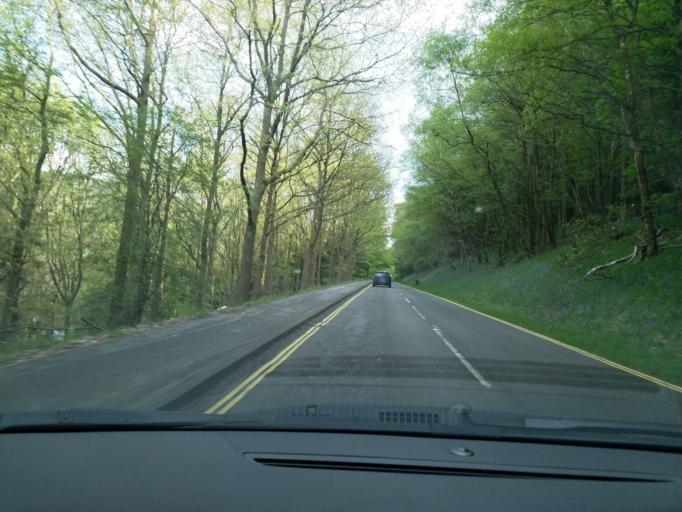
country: GB
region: England
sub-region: Derbyshire
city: Hope Valley
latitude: 53.3894
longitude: -1.7244
